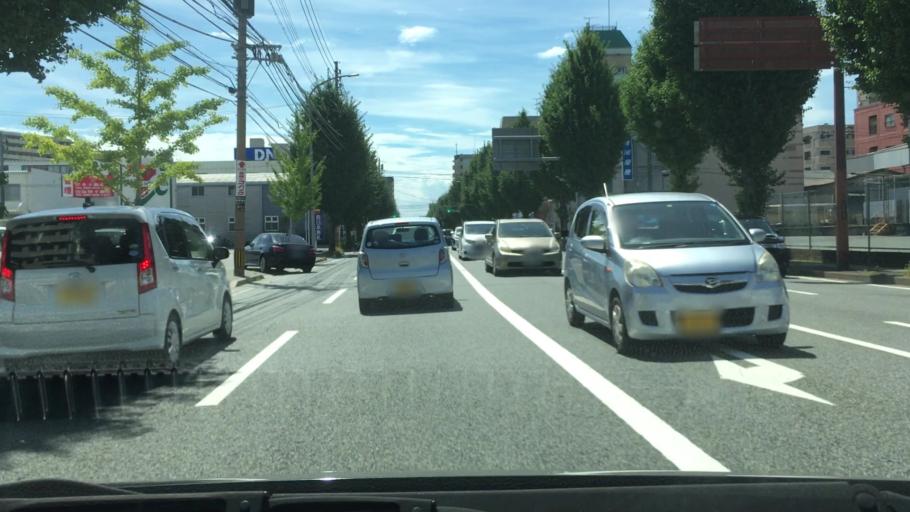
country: JP
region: Fukuoka
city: Fukuoka-shi
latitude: 33.5716
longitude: 130.4232
